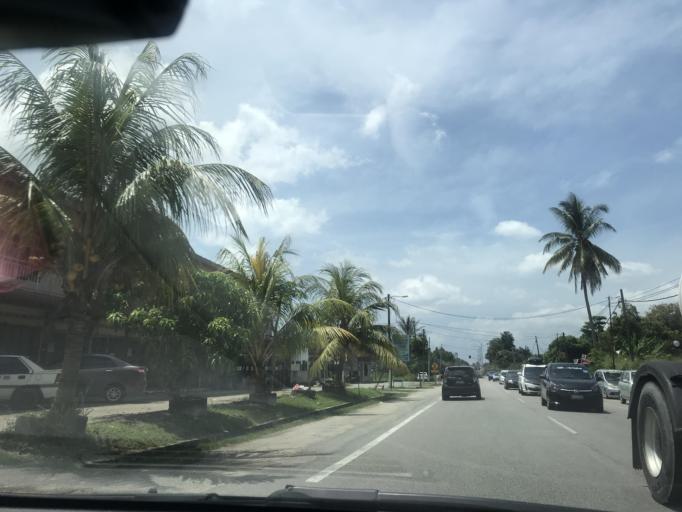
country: MY
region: Kelantan
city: Kota Bharu
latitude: 6.1475
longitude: 102.2171
